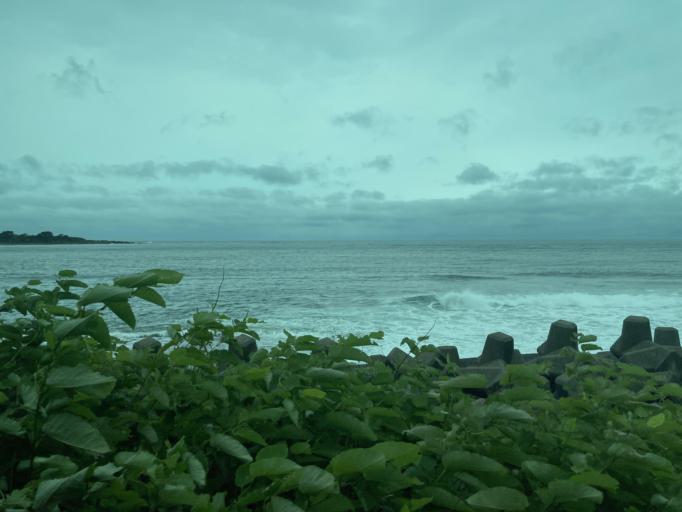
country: JP
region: Aomori
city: Shimokizukuri
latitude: 40.6713
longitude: 139.9521
